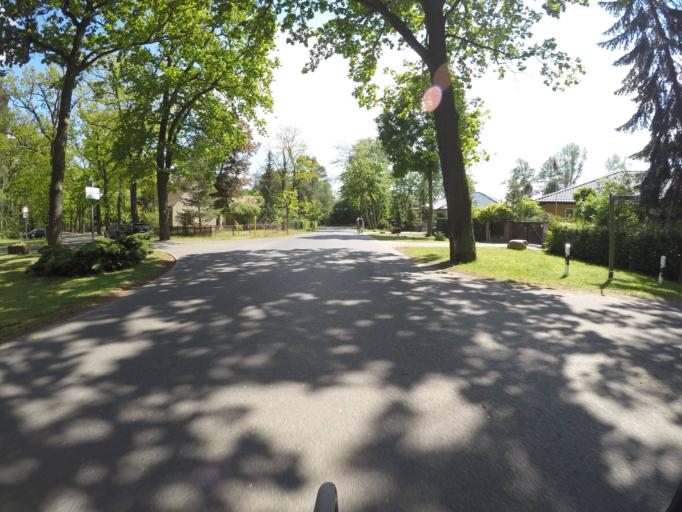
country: DE
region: Brandenburg
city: Werder
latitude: 52.3866
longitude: 12.9529
